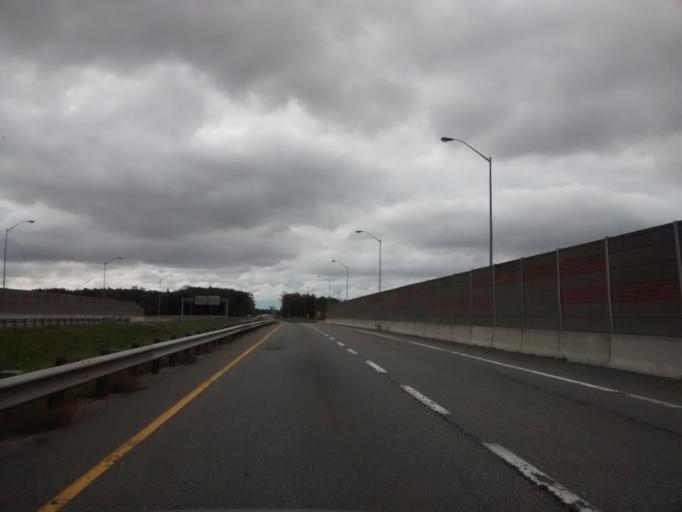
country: CA
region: Ontario
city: Ancaster
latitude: 43.2036
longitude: -79.9666
